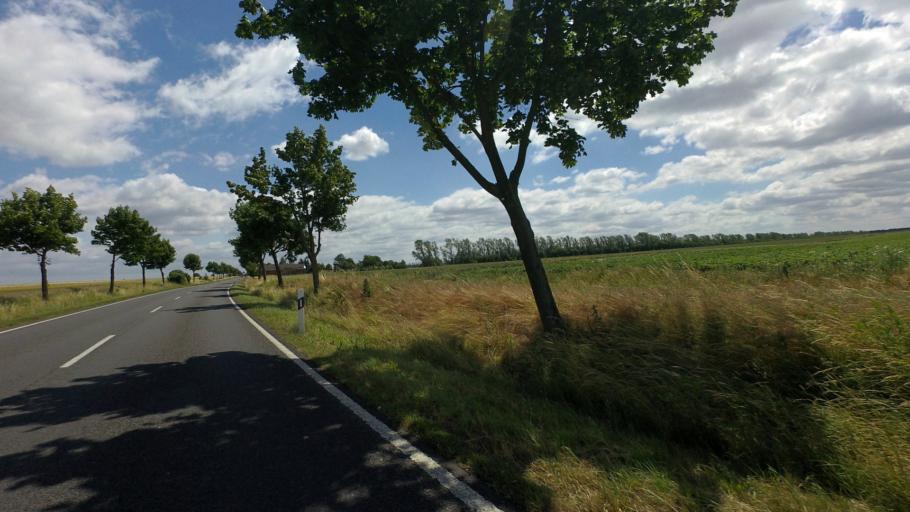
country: DE
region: Brandenburg
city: Ihlow
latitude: 51.8788
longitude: 13.3557
